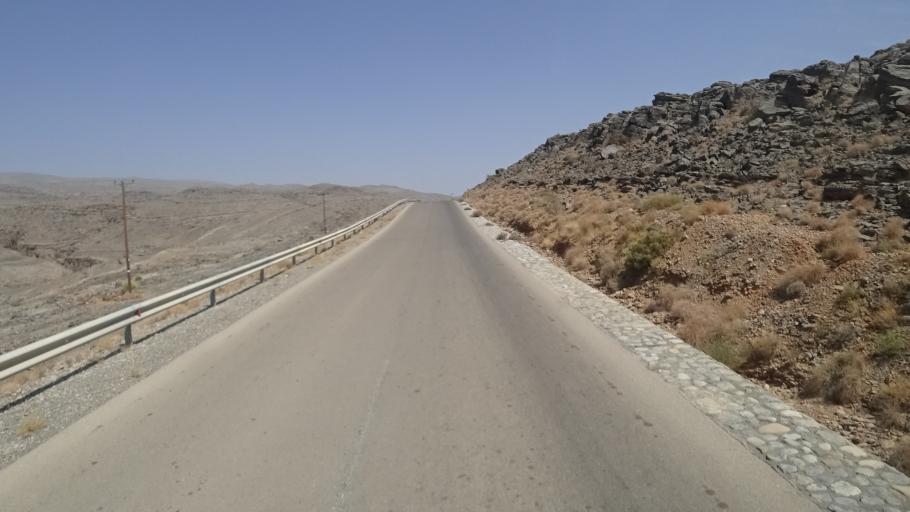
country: OM
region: Muhafazat ad Dakhiliyah
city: Bahla'
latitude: 23.0990
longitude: 57.3764
